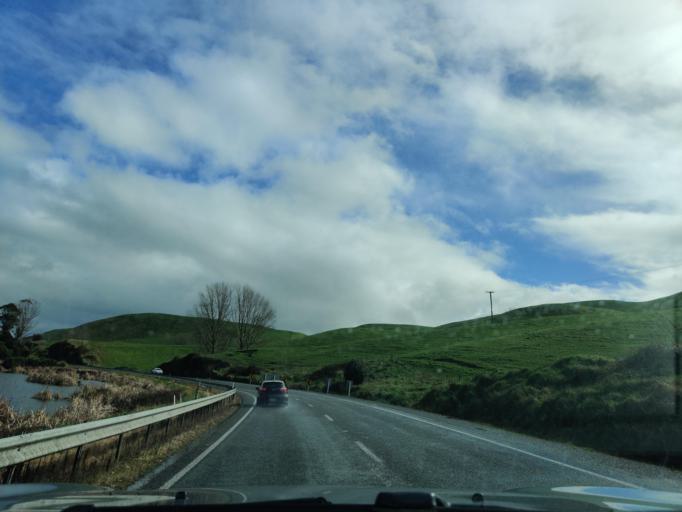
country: NZ
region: Hawke's Bay
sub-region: Hastings District
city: Hastings
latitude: -39.7187
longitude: 176.7718
